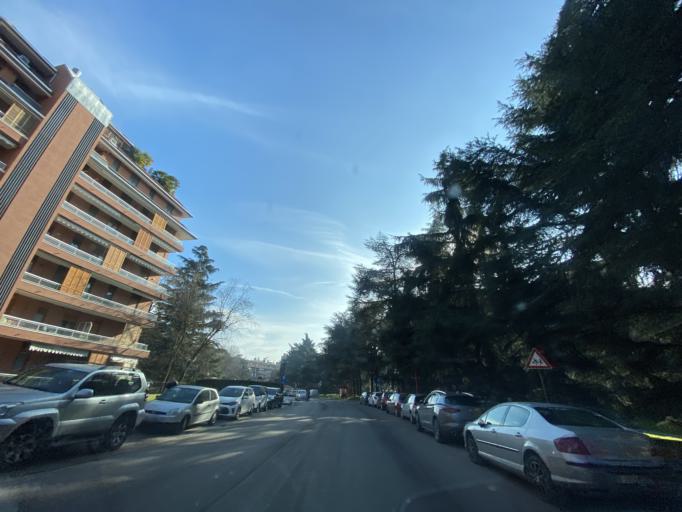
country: IT
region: Lombardy
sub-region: Citta metropolitana di Milano
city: Vimodrone
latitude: 45.5051
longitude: 9.2682
